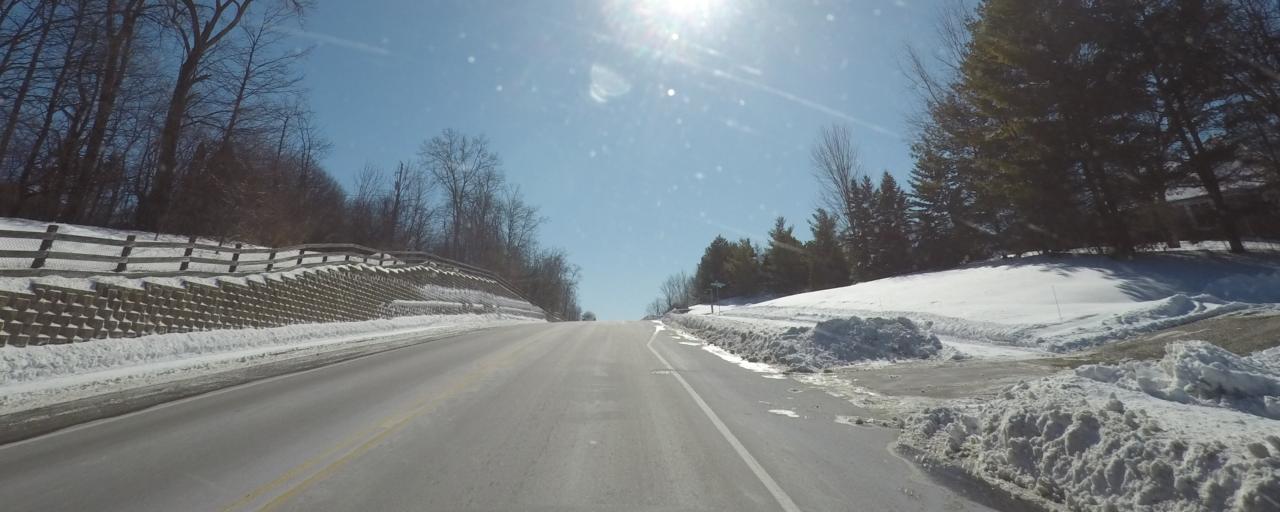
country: US
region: Wisconsin
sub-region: Waukesha County
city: Brookfield
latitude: 43.0217
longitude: -88.1470
